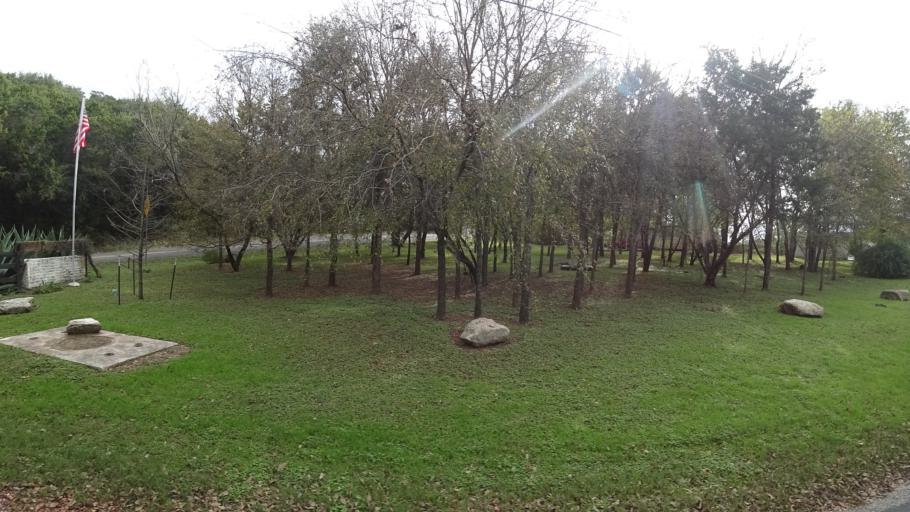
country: US
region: Texas
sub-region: Travis County
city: Hudson Bend
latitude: 30.3837
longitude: -97.9104
